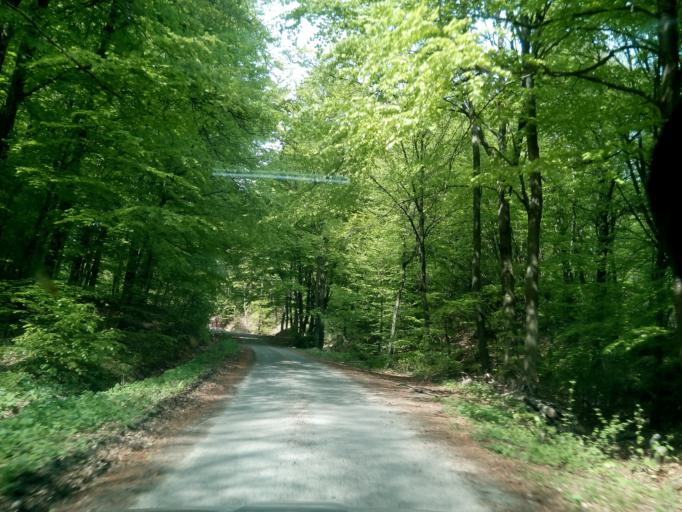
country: SK
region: Presovsky
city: Giraltovce
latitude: 48.9666
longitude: 21.4949
